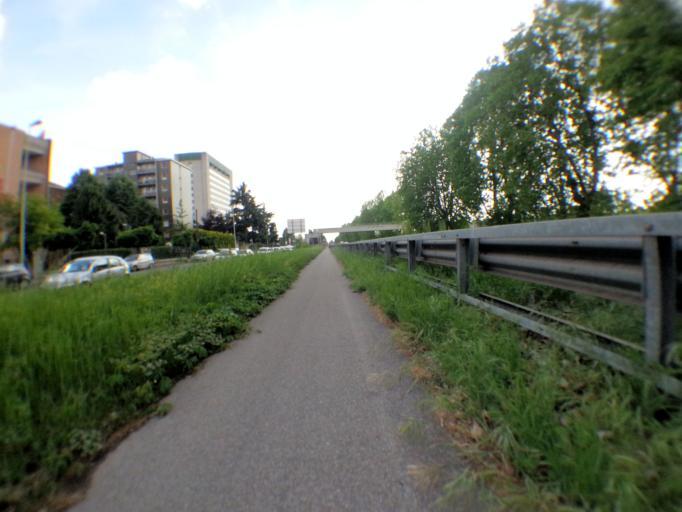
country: IT
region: Lombardy
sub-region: Citta metropolitana di Milano
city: Sesto San Giovanni
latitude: 45.5383
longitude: 9.2190
